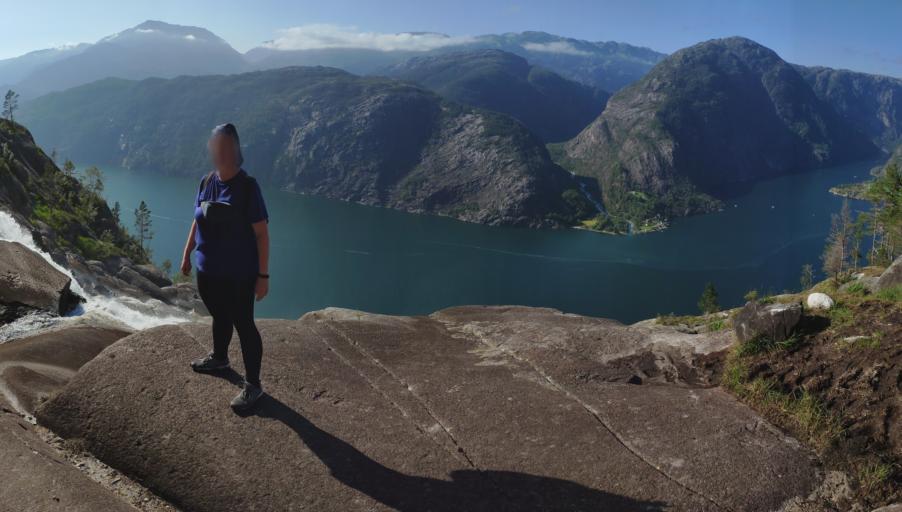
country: NO
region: Rogaland
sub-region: Sauda
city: Sauda
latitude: 59.8426
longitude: 6.3415
